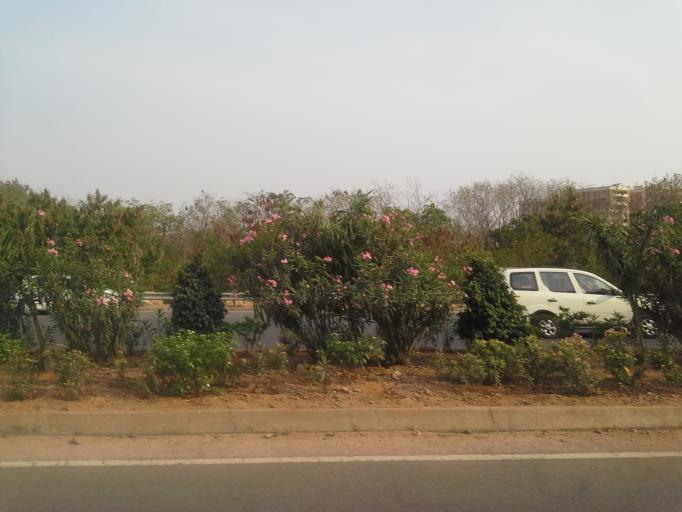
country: IN
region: Telangana
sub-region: Rangareddi
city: Kukatpalli
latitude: 17.4357
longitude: 78.3616
